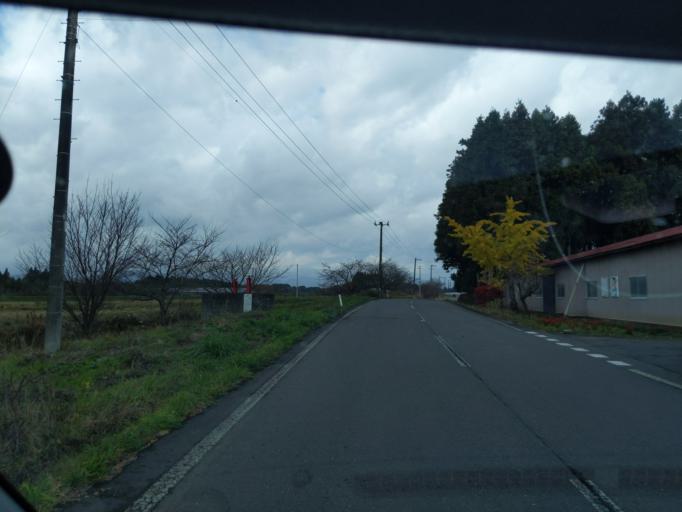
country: JP
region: Iwate
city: Mizusawa
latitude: 39.0666
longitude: 141.0793
